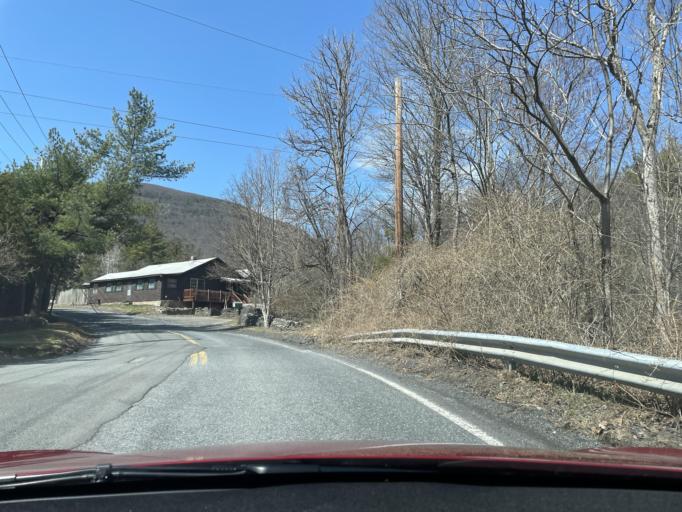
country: US
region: New York
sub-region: Ulster County
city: Manorville
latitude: 42.1129
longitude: -74.0476
